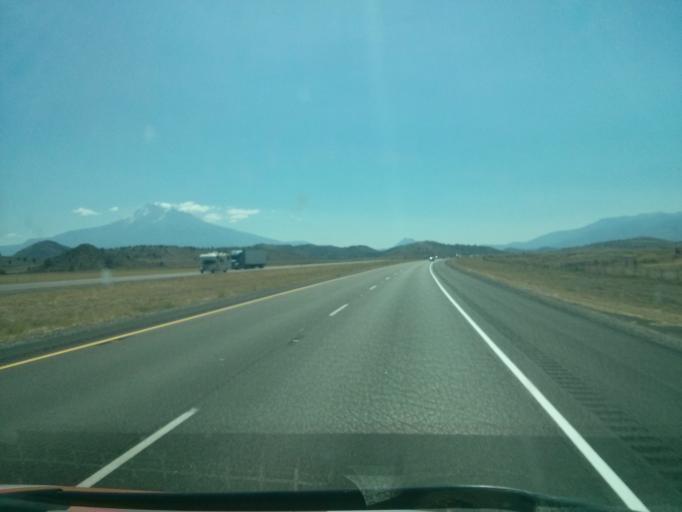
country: US
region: California
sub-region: Siskiyou County
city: Montague
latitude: 41.6220
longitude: -122.5175
